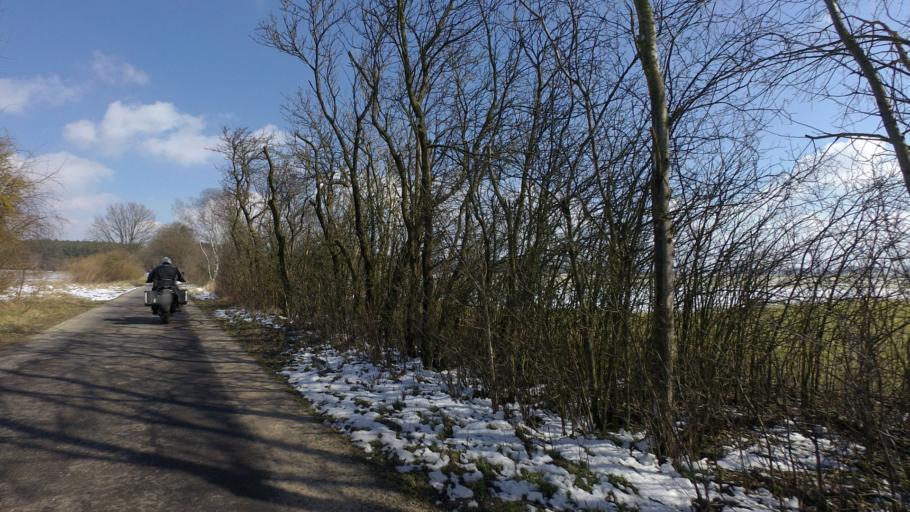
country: DE
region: Brandenburg
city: Werftpfuhl
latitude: 52.7005
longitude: 13.7817
